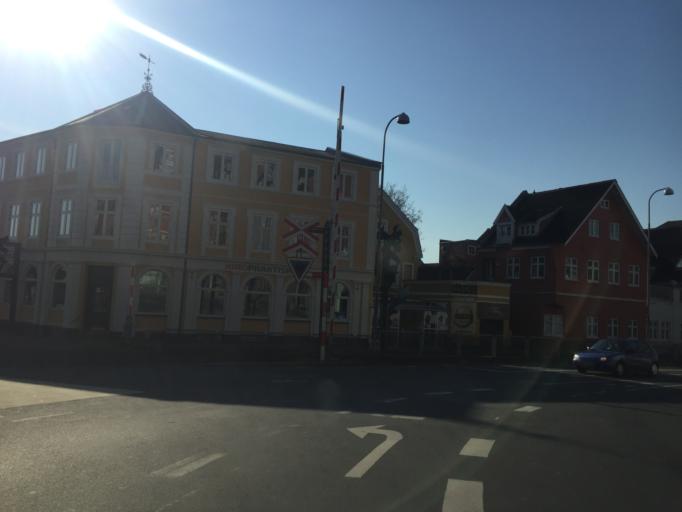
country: DK
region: South Denmark
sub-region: Svendborg Kommune
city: Svendborg
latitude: 55.0590
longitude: 10.6116
